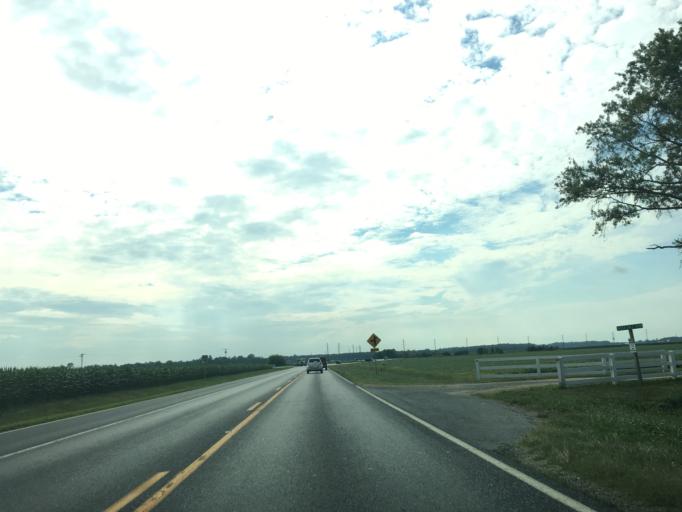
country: US
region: Delaware
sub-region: Sussex County
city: Bridgeville
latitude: 38.7619
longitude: -75.6060
